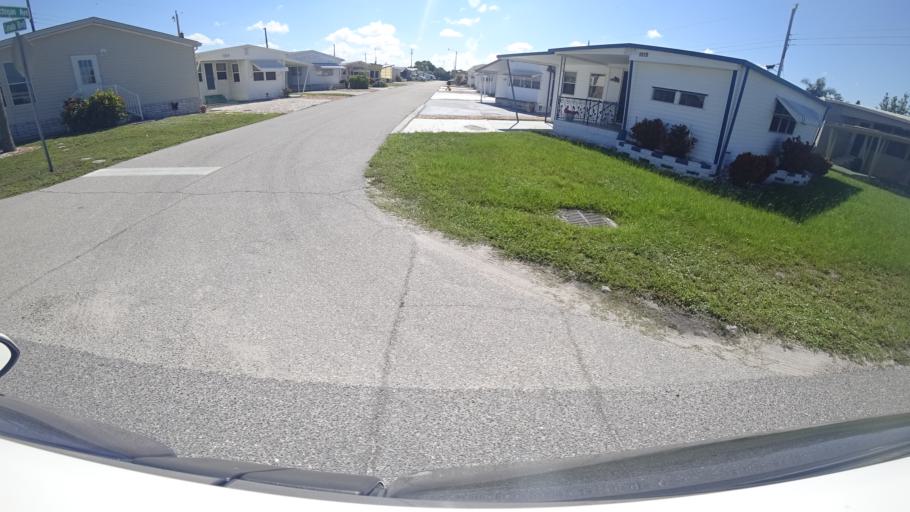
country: US
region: Florida
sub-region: Manatee County
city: Bayshore Gardens
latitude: 27.4200
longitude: -82.5806
